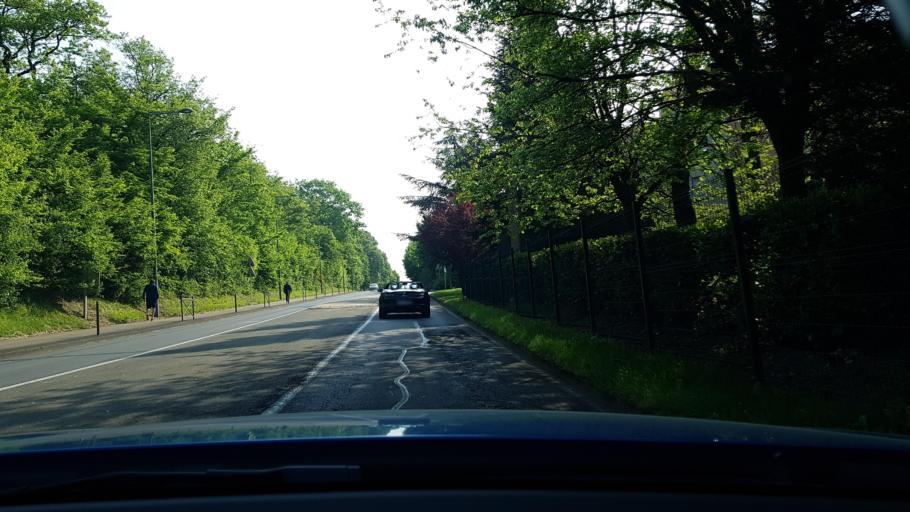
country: FR
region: Lorraine
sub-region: Departement de la Moselle
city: Terville
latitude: 49.3453
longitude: 6.1190
